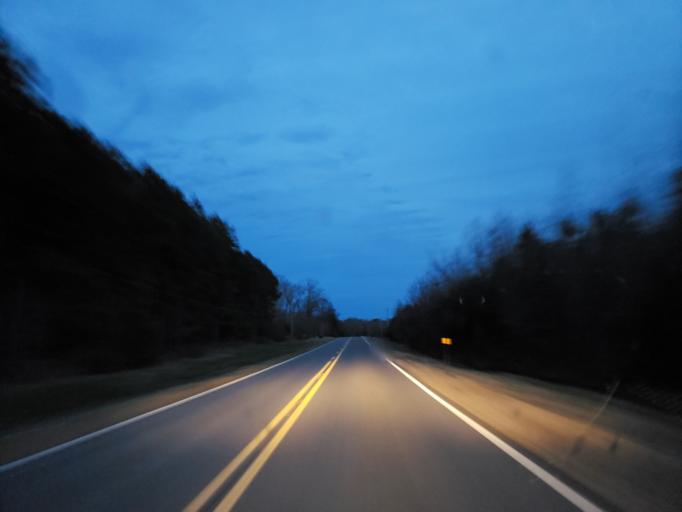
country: US
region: Alabama
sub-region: Greene County
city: Eutaw
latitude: 32.8981
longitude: -87.9633
